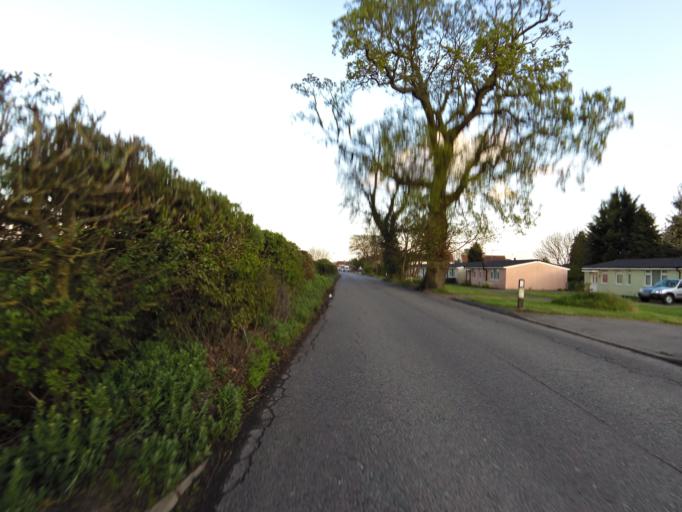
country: GB
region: England
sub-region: Suffolk
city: Ipswich
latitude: 52.0740
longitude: 1.1885
